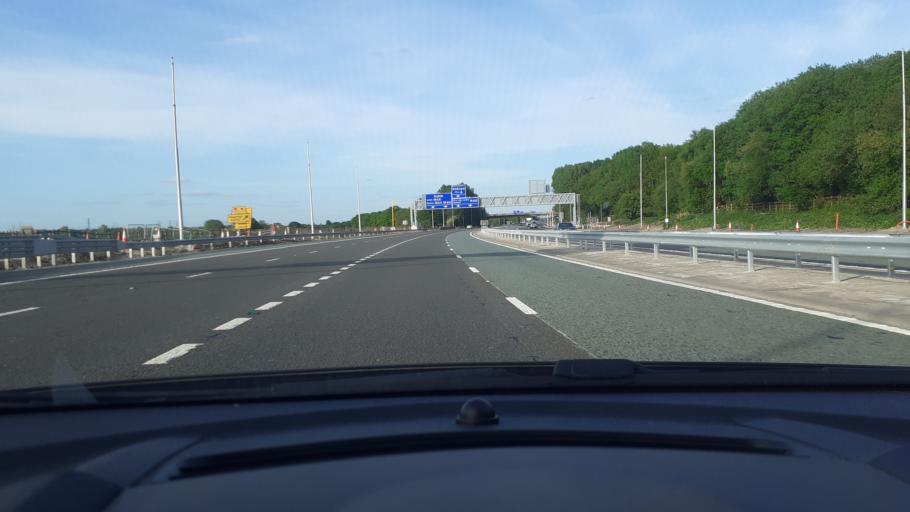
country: GB
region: England
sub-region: City and Borough of Salford
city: Walkden
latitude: 53.4816
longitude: -2.3926
